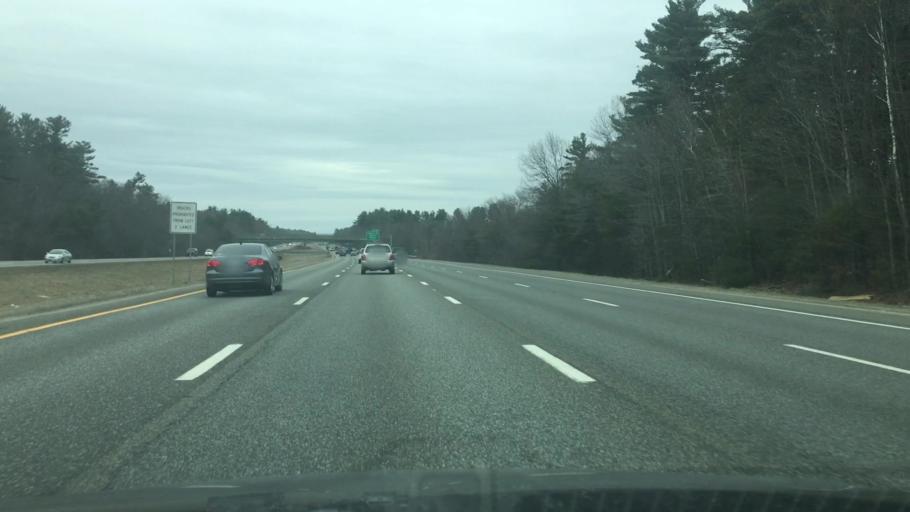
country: US
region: Massachusetts
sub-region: Essex County
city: Topsfield
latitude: 42.6375
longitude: -70.9767
